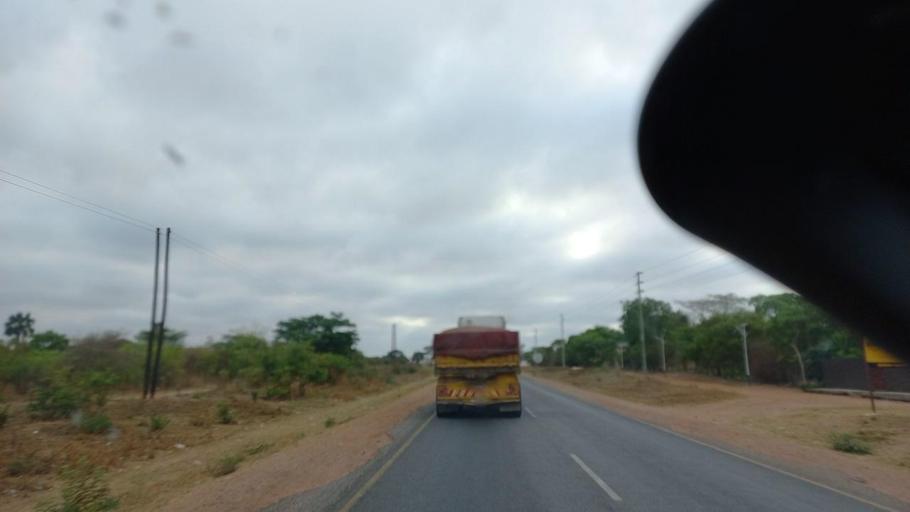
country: ZM
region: Lusaka
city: Chongwe
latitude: -15.3514
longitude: 28.5575
